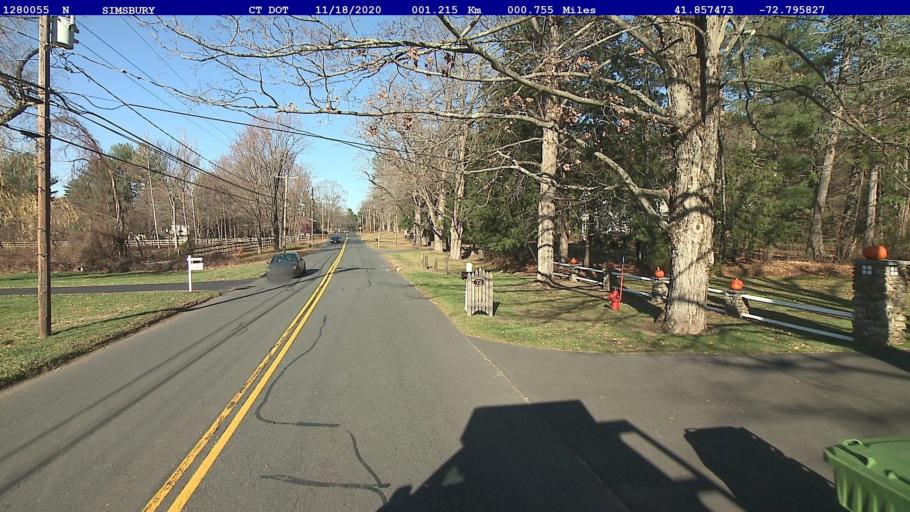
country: US
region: Connecticut
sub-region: Hartford County
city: Simsbury Center
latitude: 41.8575
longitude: -72.7958
